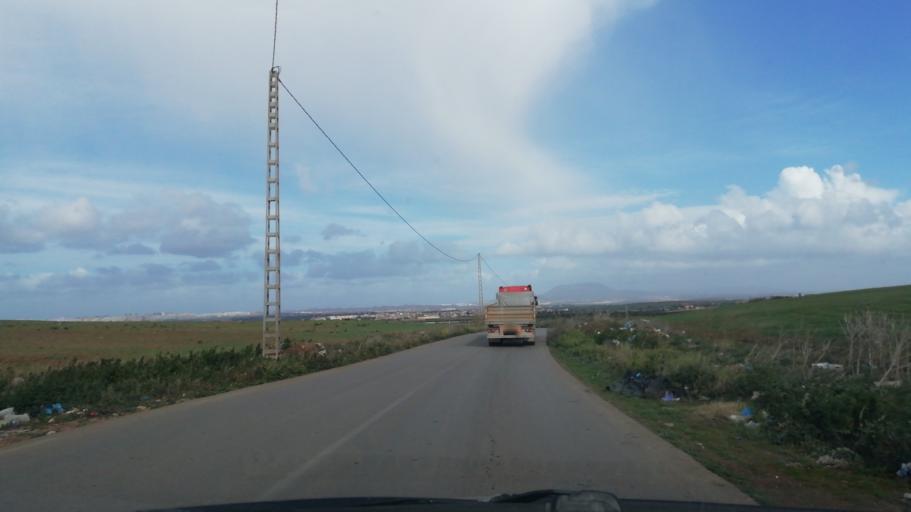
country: DZ
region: Oran
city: Sidi ech Chahmi
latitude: 35.6379
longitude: -0.5193
